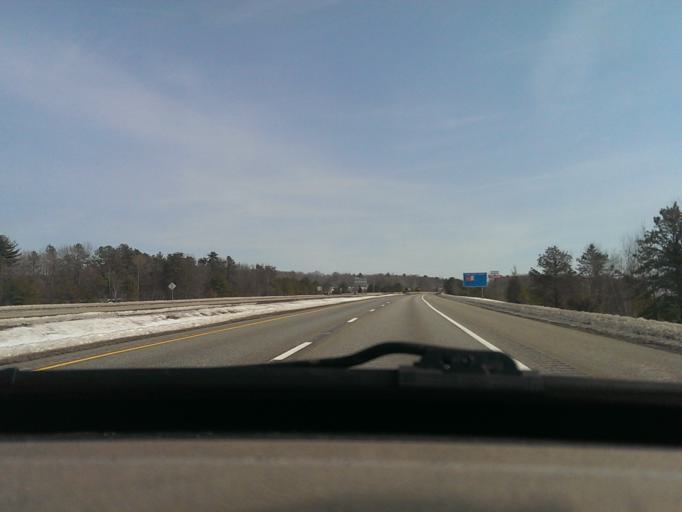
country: US
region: Massachusetts
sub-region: Worcester County
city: Millville
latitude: 42.0259
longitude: -71.6082
